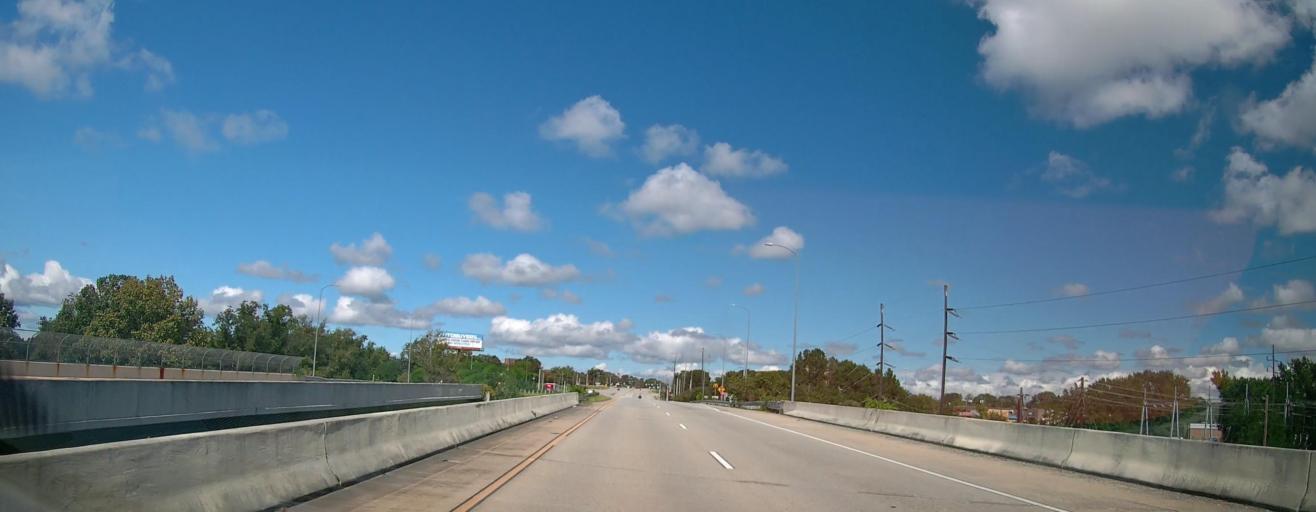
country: US
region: Georgia
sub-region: Bibb County
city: Macon
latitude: 32.8032
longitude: -83.5685
